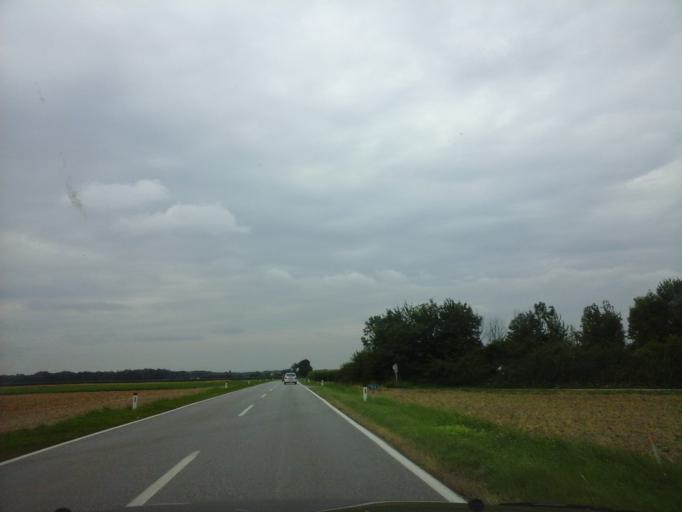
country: AT
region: Lower Austria
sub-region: Politischer Bezirk Ganserndorf
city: Orth an der Donau
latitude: 48.1538
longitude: 16.7325
